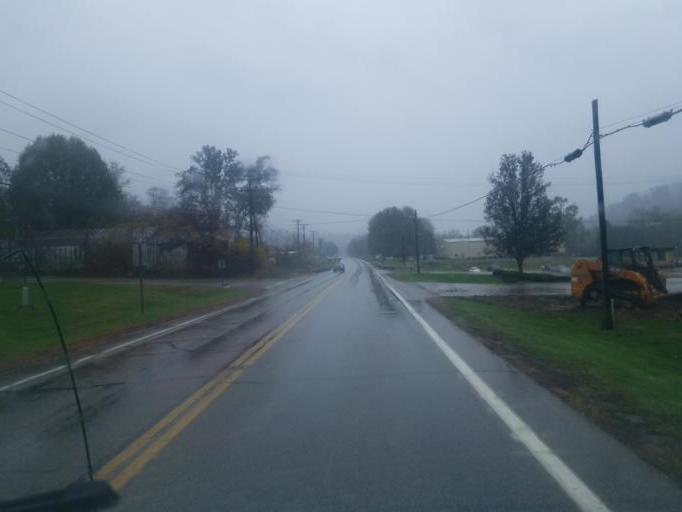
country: US
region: Ohio
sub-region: Morgan County
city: McConnelsville
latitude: 39.6761
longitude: -81.8809
